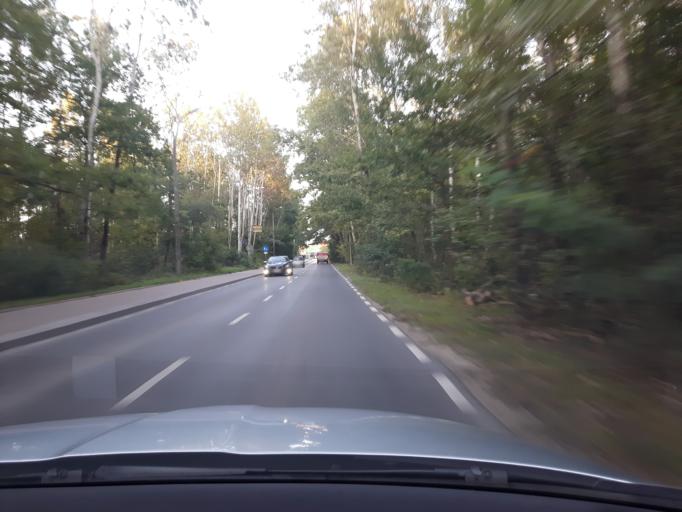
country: PL
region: Masovian Voivodeship
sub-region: Powiat wolominski
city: Kobylka
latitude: 52.3340
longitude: 21.1746
